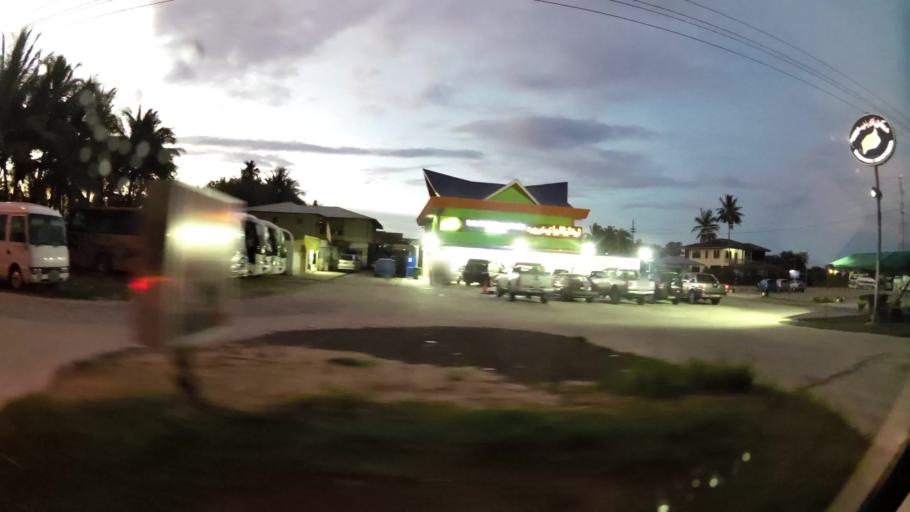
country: BN
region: Belait
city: Seria
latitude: 4.6531
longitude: 114.4279
